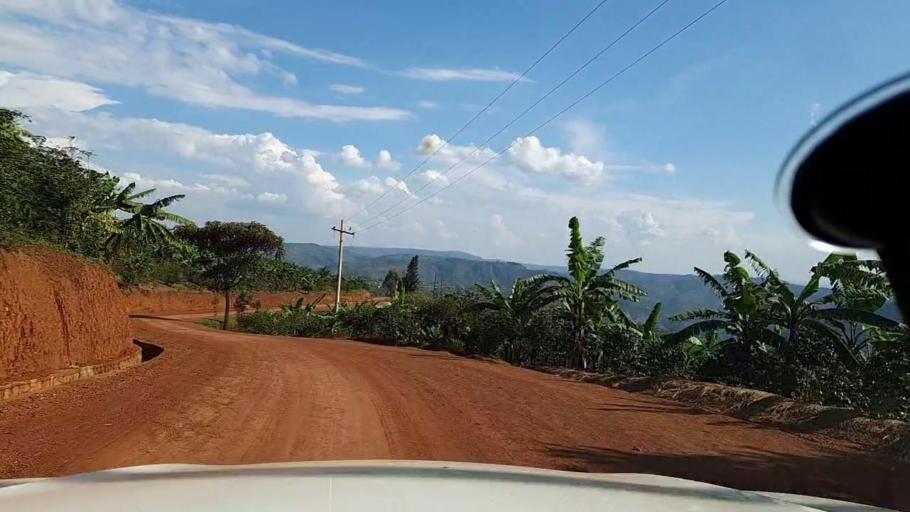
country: RW
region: Kigali
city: Kigali
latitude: -1.8346
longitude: 29.8457
